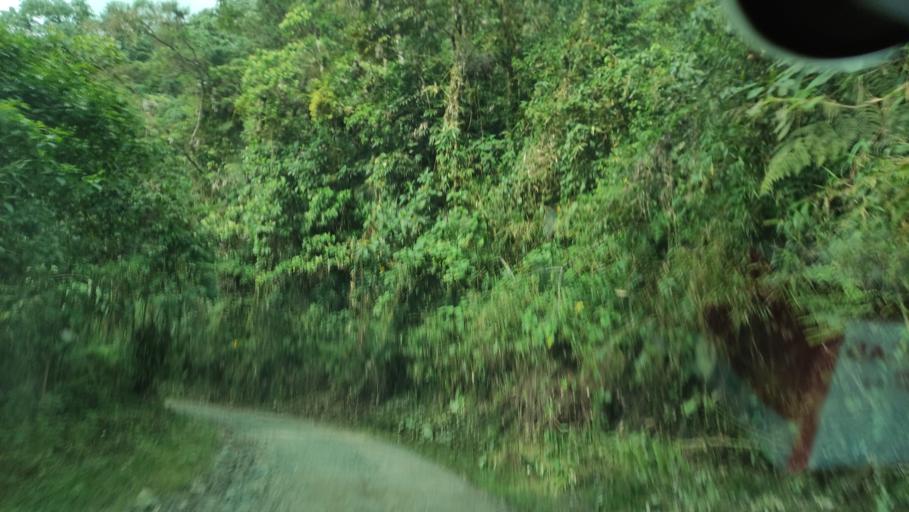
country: CO
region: Valle del Cauca
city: San Pedro
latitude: 3.8810
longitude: -76.1541
